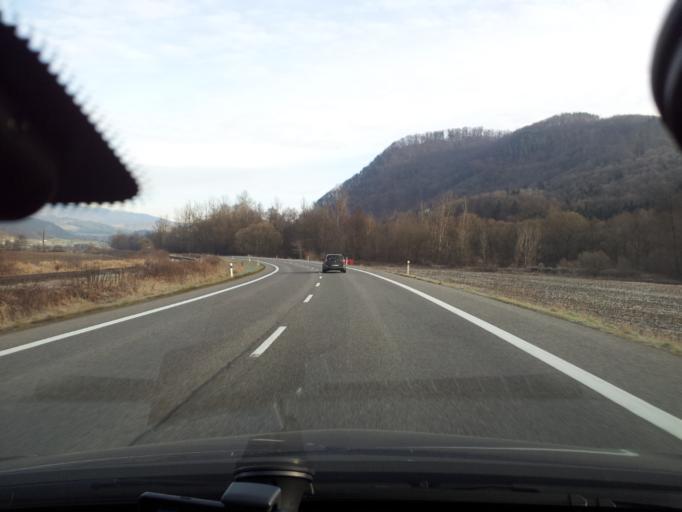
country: SK
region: Banskobystricky
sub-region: Okres Banska Bystrica
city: Banska Bystrica
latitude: 48.7471
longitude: 19.2510
